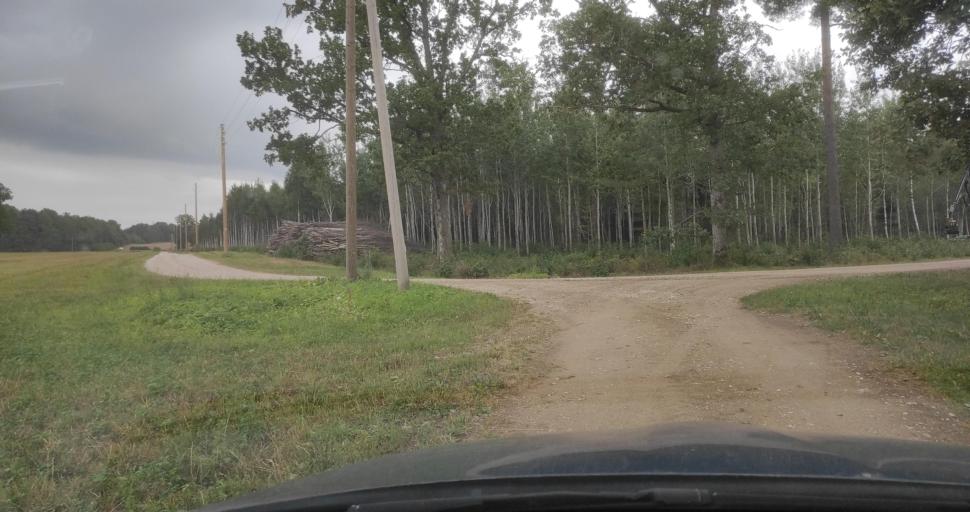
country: LV
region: Durbe
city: Liegi
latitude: 56.7050
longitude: 21.3599
